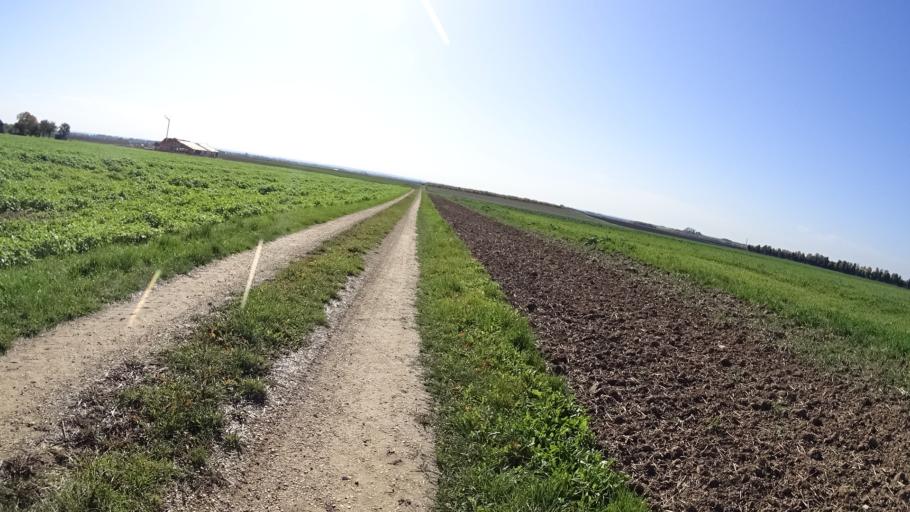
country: DE
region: Bavaria
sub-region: Upper Bavaria
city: Gaimersheim
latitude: 48.8335
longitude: 11.3510
